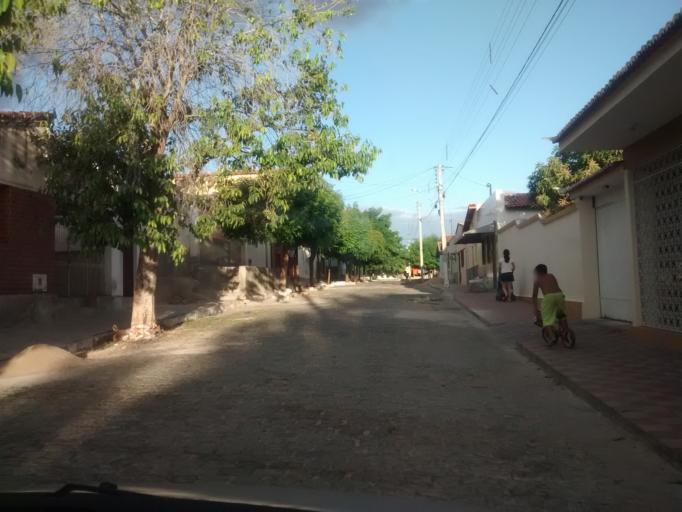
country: BR
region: Rio Grande do Norte
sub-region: Caico
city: Caico
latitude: -6.4699
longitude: -37.0990
